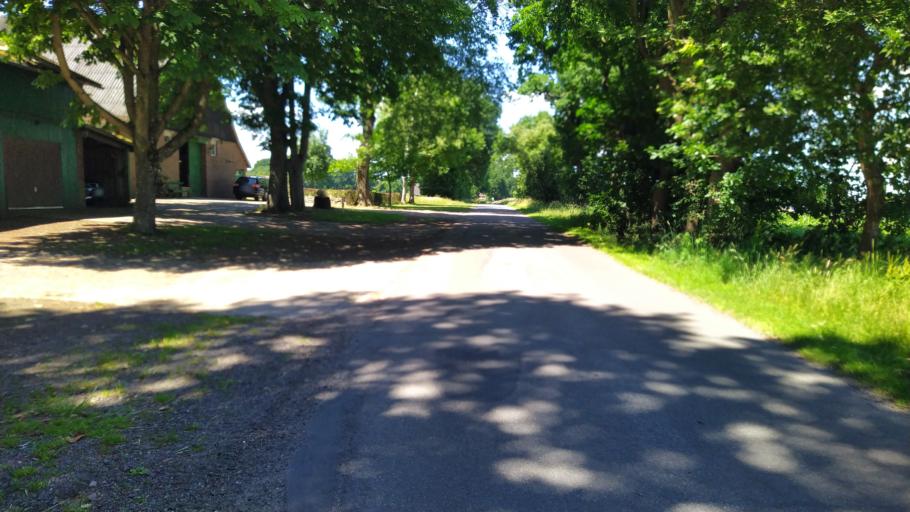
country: DE
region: Lower Saxony
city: Estorf
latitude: 53.5672
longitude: 9.2067
